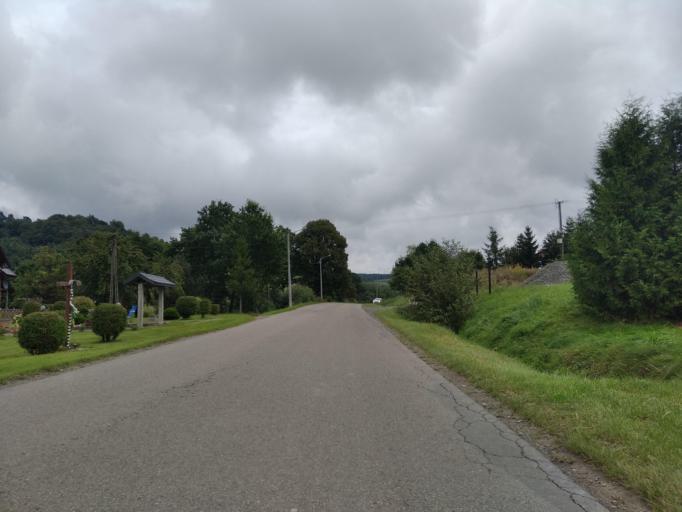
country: PL
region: Subcarpathian Voivodeship
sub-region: Powiat brzozowski
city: Nozdrzec
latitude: 49.7288
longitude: 22.2760
